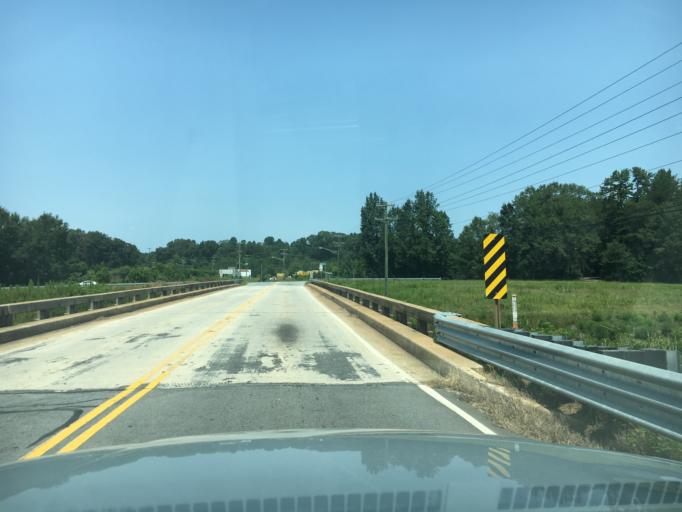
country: US
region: South Carolina
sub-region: Pickens County
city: Central
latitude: 34.7058
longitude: -82.7577
